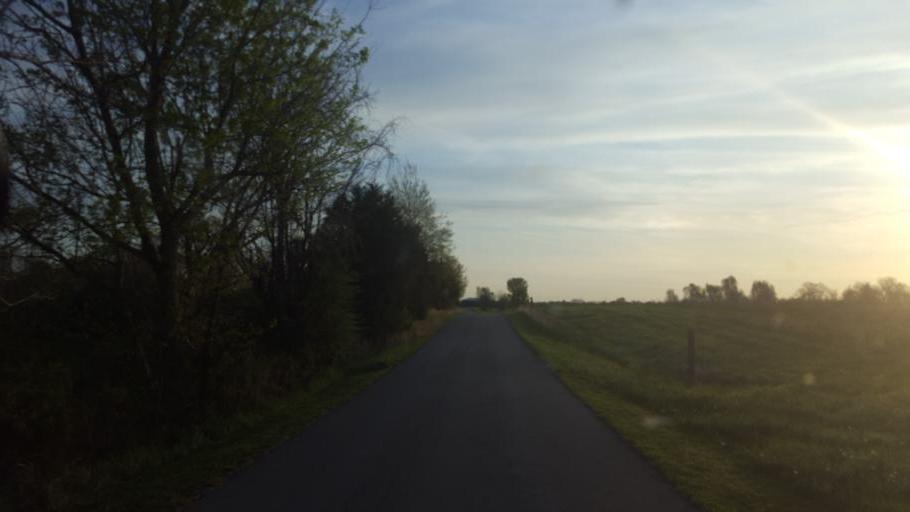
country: US
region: Kentucky
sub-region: Barren County
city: Cave City
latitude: 37.1639
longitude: -86.0106
